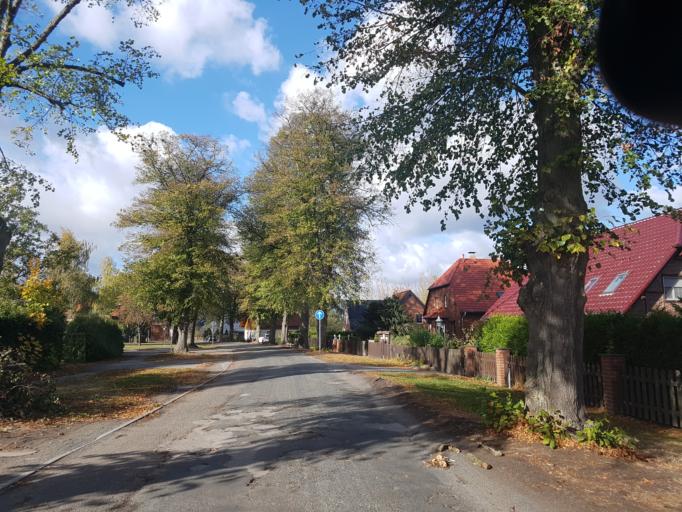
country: DE
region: Brandenburg
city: Nauen
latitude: 52.6631
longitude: 12.9093
